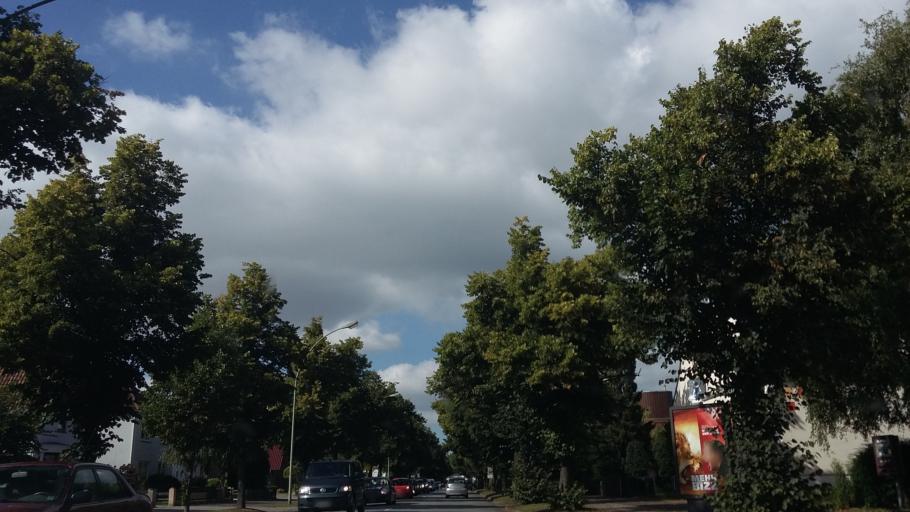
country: DE
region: Lower Saxony
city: Loxstedt
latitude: 53.4968
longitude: 8.6013
